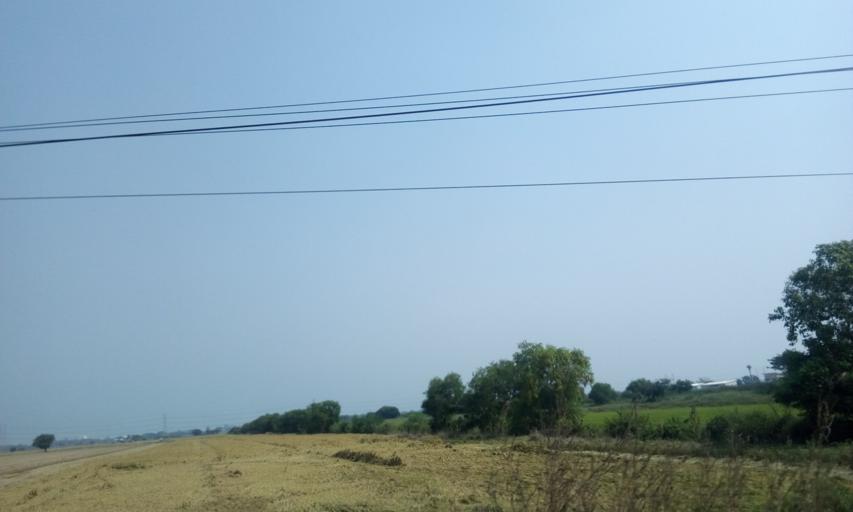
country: TH
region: Pathum Thani
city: Ban Lam Luk Ka
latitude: 13.9814
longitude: 100.7544
